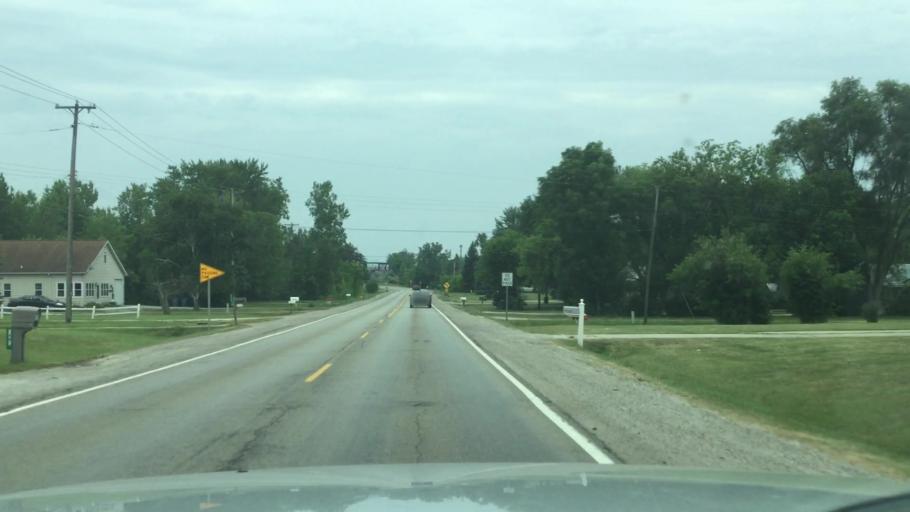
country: US
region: Michigan
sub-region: Genesee County
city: Flint
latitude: 42.9483
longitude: -83.7123
